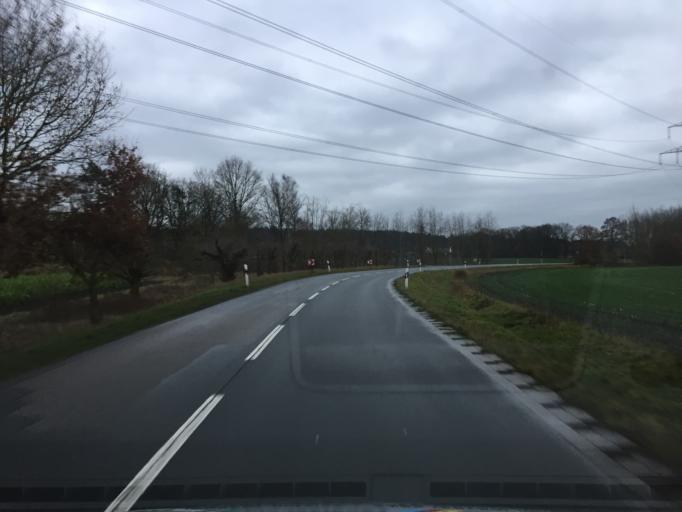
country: DE
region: Lower Saxony
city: Pennigsehl
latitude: 52.6223
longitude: 8.9967
